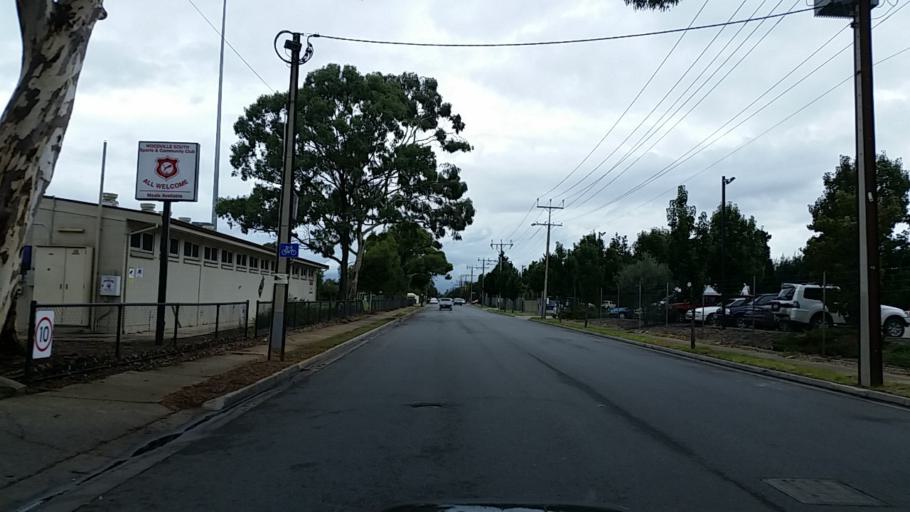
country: AU
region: South Australia
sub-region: Charles Sturt
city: Findon
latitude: -34.8974
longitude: 138.5415
